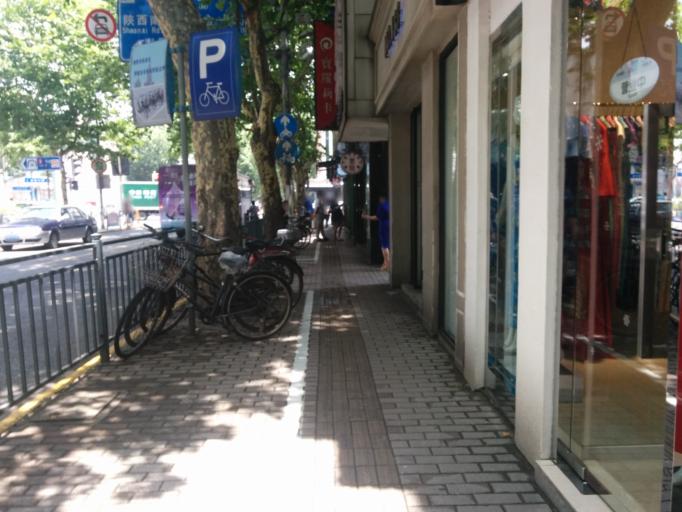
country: CN
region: Shanghai Shi
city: Shanghai
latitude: 31.2192
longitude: 121.4568
